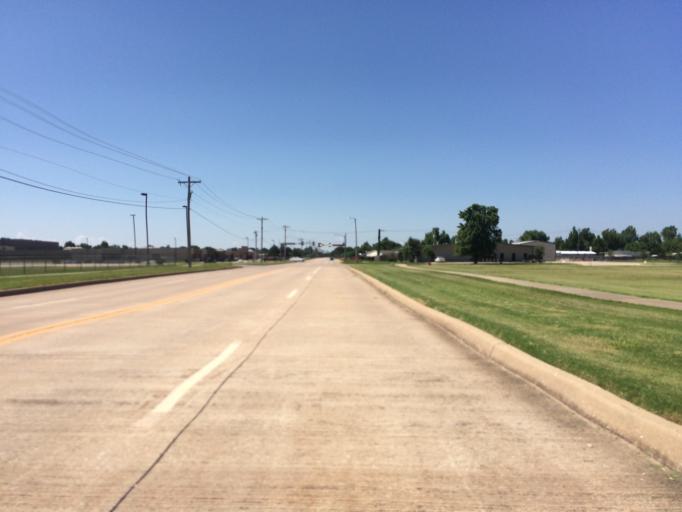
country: US
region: Oklahoma
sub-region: Cleveland County
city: Norman
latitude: 35.2437
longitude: -97.4501
